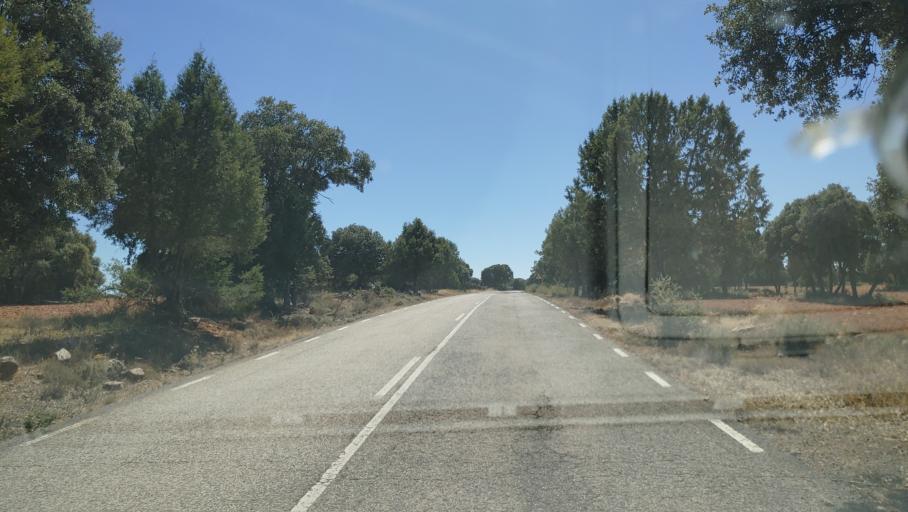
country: ES
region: Castille-La Mancha
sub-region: Provincia de Albacete
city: Ossa de Montiel
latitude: 38.8883
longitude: -2.7710
